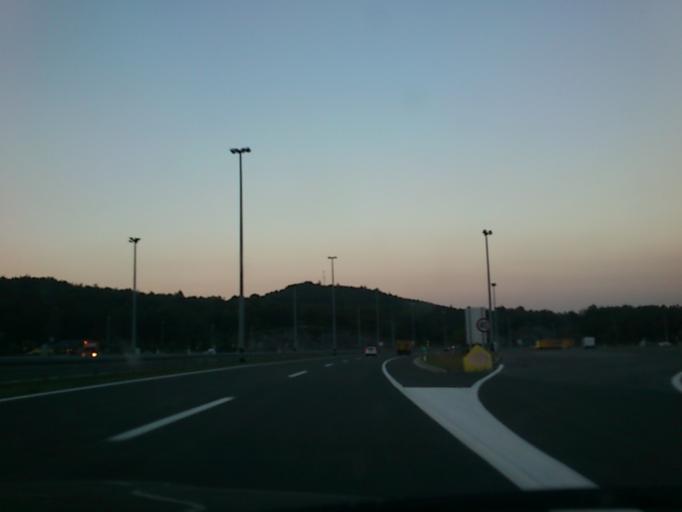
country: HR
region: Karlovacka
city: Ostarije
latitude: 45.1290
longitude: 15.2451
